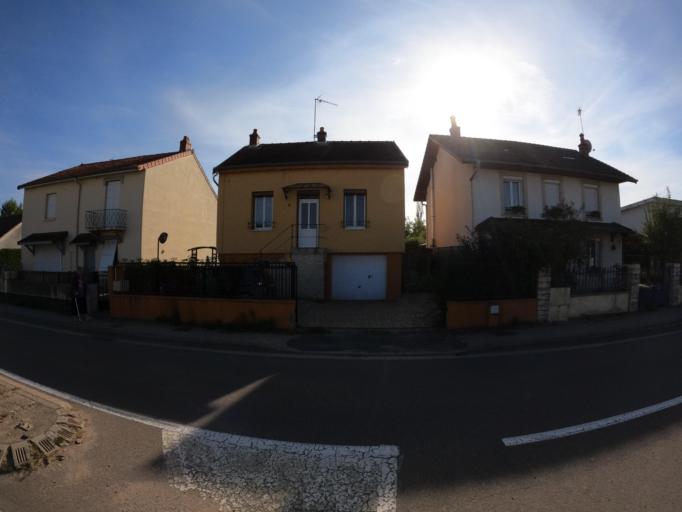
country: FR
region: Franche-Comte
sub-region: Departement du Jura
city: Bletterans
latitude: 46.7493
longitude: 5.4562
